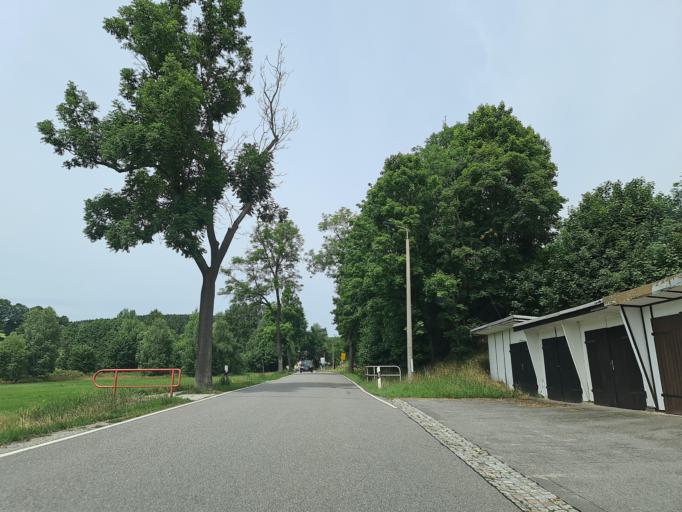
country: DE
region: Saxony
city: Heidersdorf
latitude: 50.6670
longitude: 13.4200
